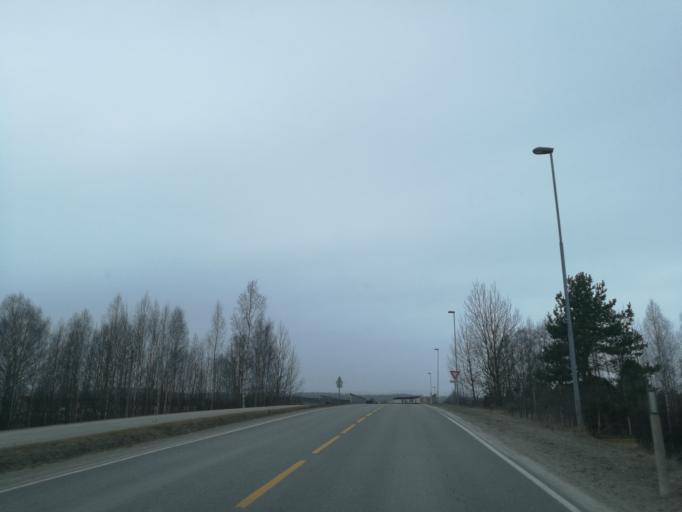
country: NO
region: Hedmark
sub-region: Grue
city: Kirkenaer
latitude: 60.4511
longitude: 12.0598
